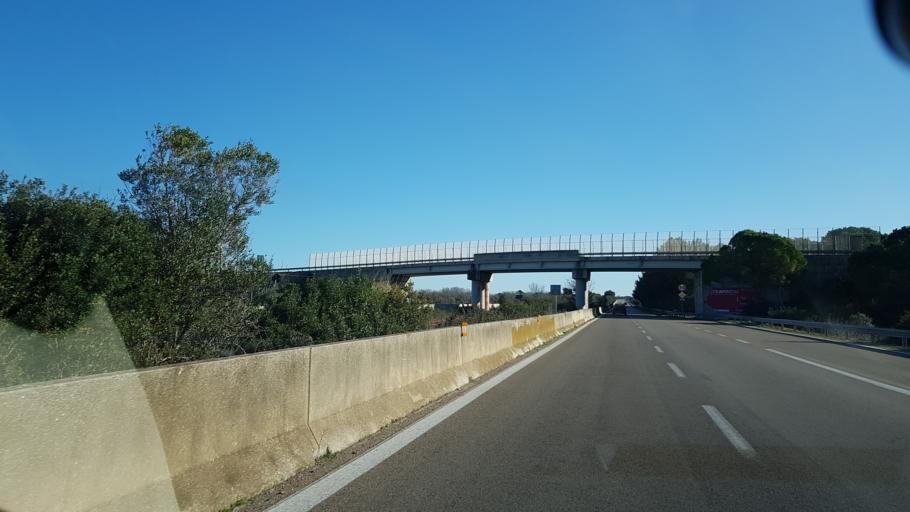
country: IT
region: Apulia
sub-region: Provincia di Lecce
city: Taviano
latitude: 40.0128
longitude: 18.0502
